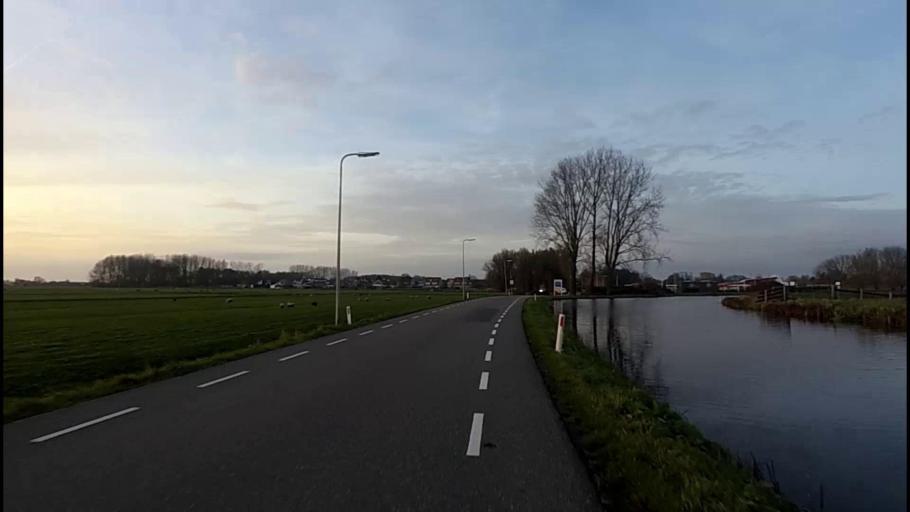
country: NL
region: South Holland
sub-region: Gemeente Vlist
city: Haastrecht
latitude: 51.9925
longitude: 4.7833
